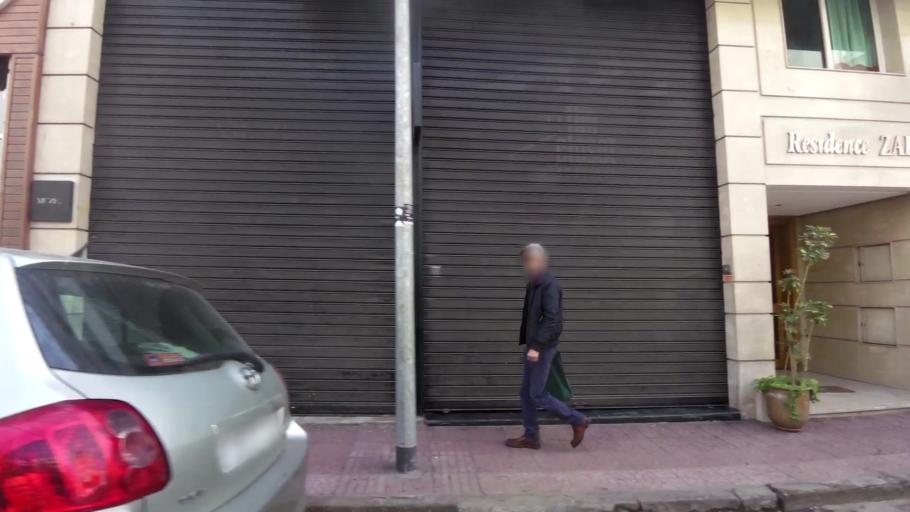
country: MA
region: Grand Casablanca
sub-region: Casablanca
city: Casablanca
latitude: 33.5937
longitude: -7.6428
